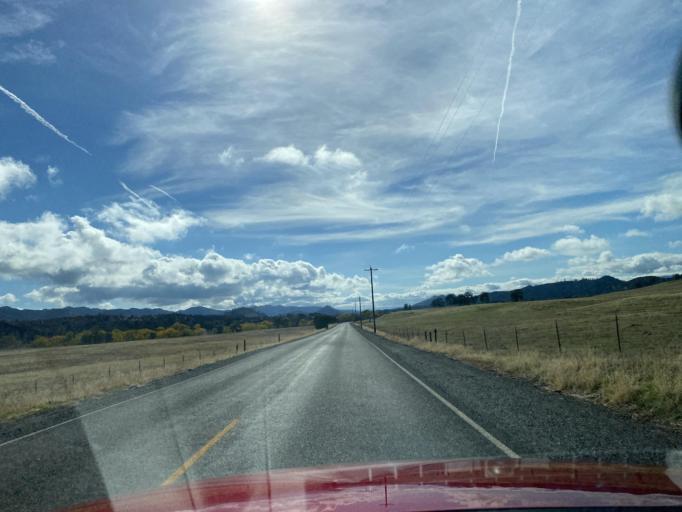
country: US
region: California
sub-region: Glenn County
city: Willows
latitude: 39.4688
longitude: -122.5123
